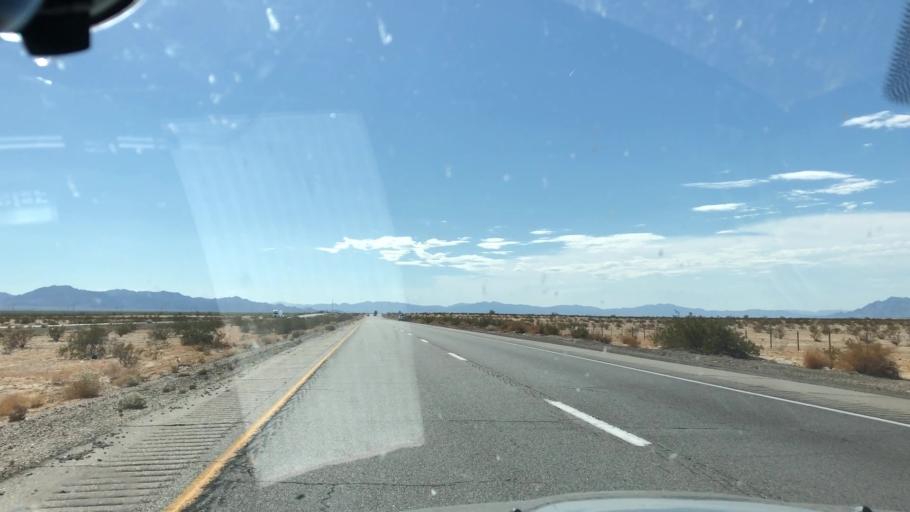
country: US
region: California
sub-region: Riverside County
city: Mesa Verde
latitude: 33.6425
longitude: -115.1070
